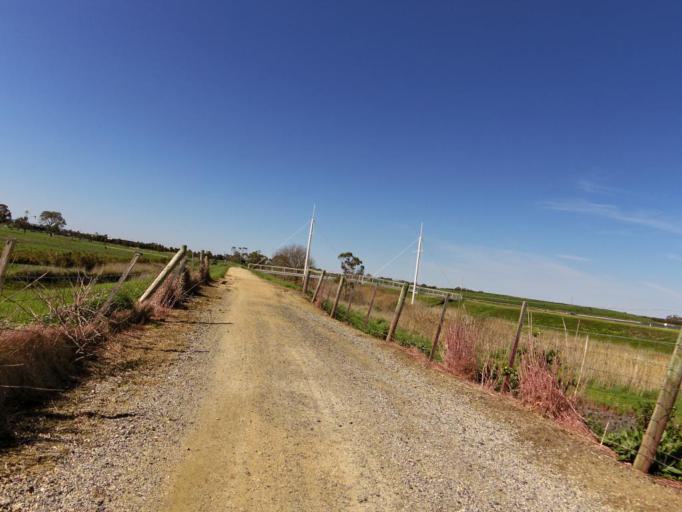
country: AU
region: Victoria
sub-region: Kingston
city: Patterson Lakes
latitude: -38.0402
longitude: 145.1790
